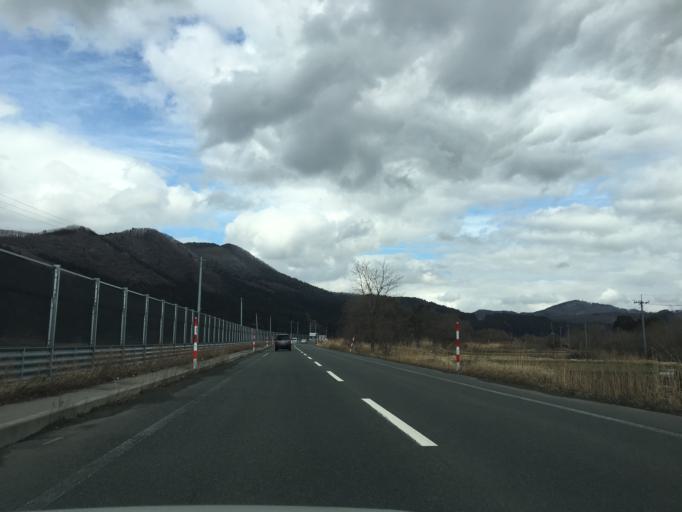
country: JP
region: Akita
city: Hanawa
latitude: 40.2272
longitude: 140.6794
